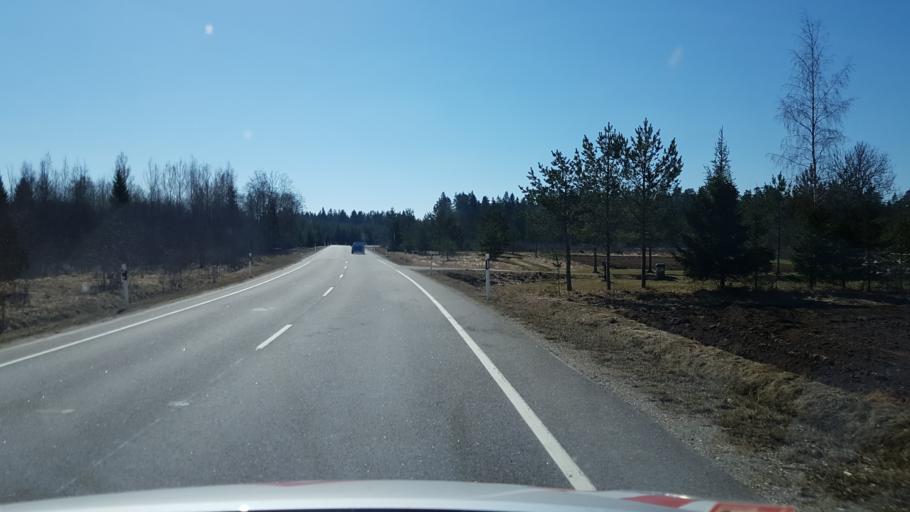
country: EE
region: Laeaene-Virumaa
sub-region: Vinni vald
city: Vinni
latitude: 59.1427
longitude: 26.5962
